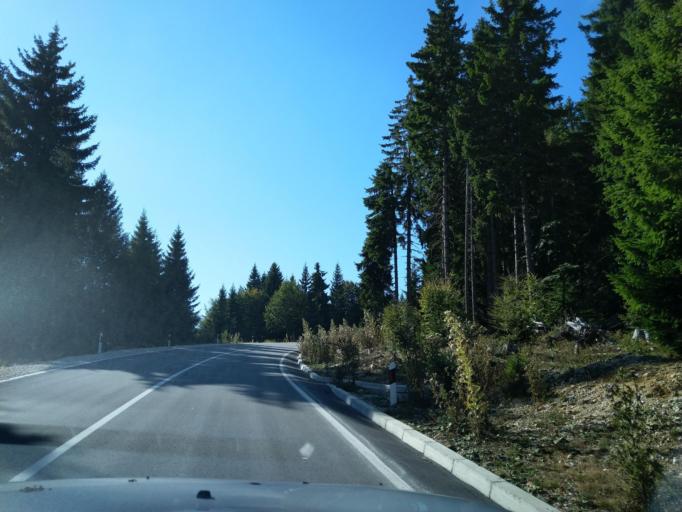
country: RS
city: Sokolovica
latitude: 43.3026
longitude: 20.3076
